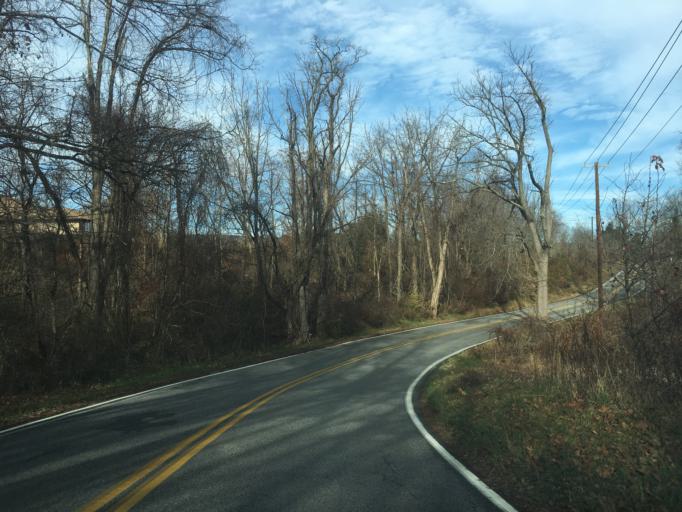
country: US
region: Pennsylvania
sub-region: Dauphin County
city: Colonial Park
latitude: 40.3259
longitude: -76.8409
